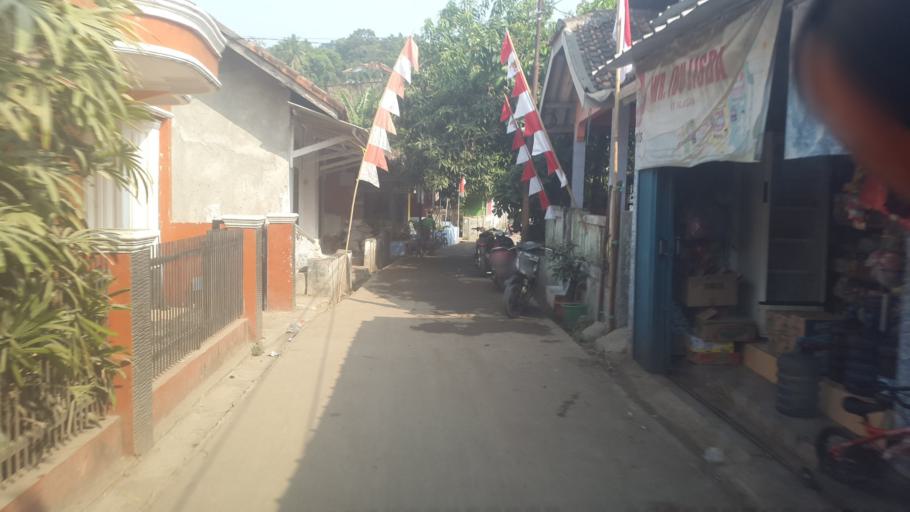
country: ID
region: West Java
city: Tugu
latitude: -6.9520
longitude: 106.4408
